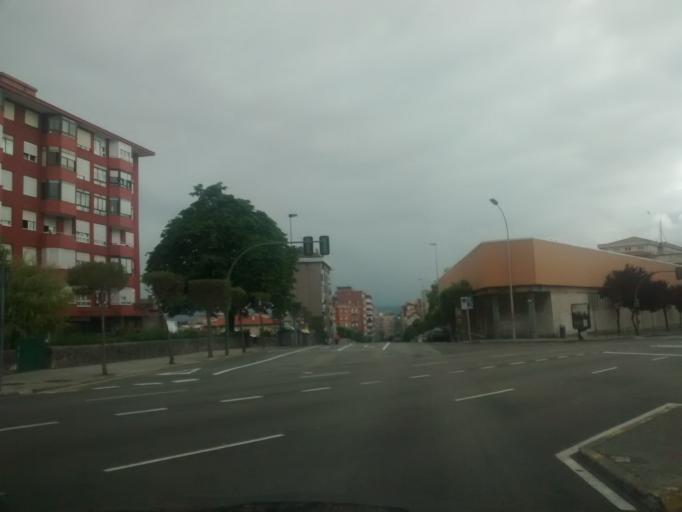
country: ES
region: Cantabria
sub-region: Provincia de Cantabria
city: Santander
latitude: 43.4637
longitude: -3.8225
